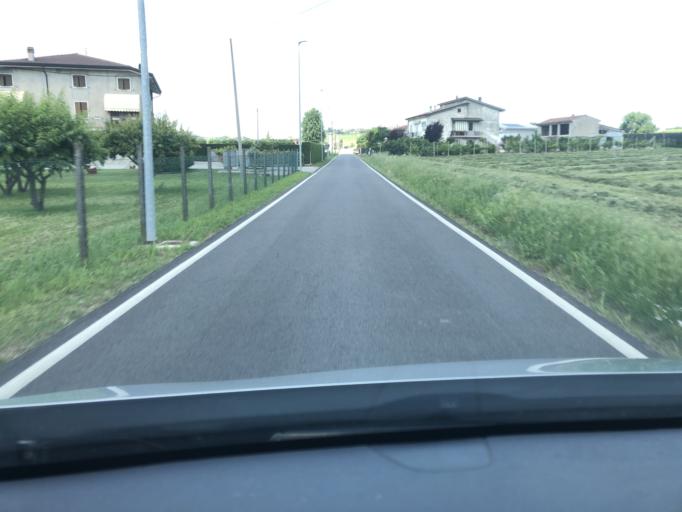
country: IT
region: Veneto
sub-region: Provincia di Verona
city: Rosegaferro
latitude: 45.3600
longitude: 10.8110
